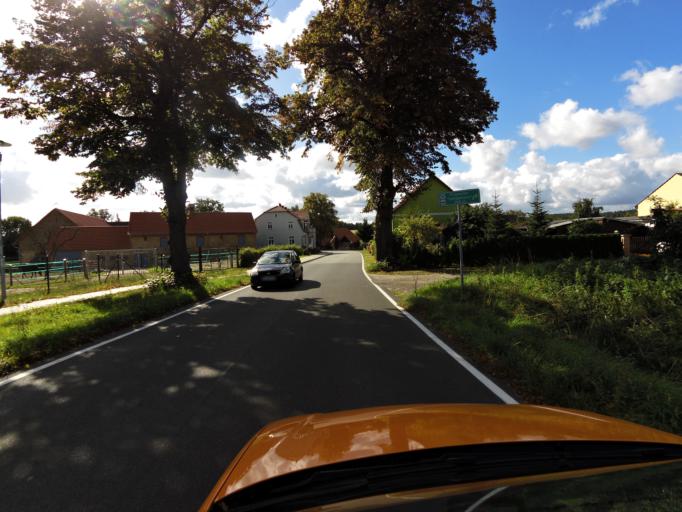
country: DE
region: Brandenburg
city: Michendorf
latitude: 52.2712
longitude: 13.0736
